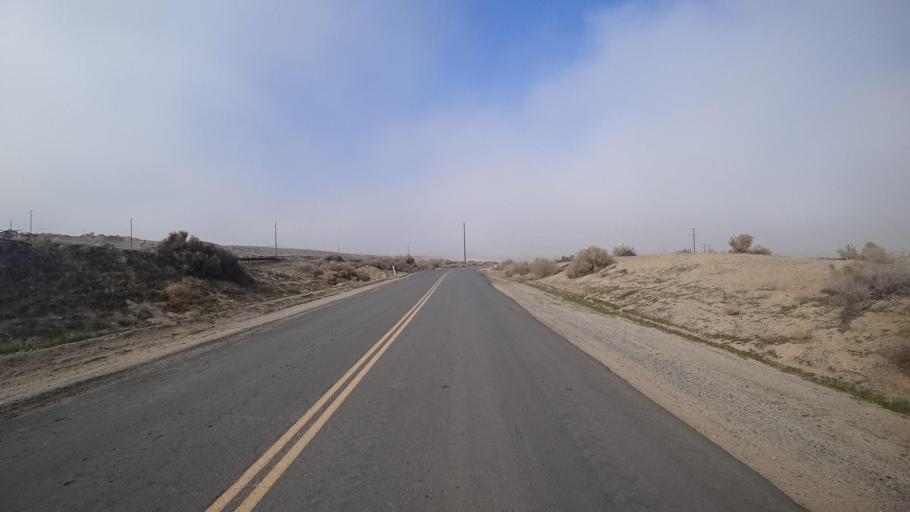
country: US
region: California
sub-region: Kern County
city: Ford City
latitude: 35.1729
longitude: -119.4249
